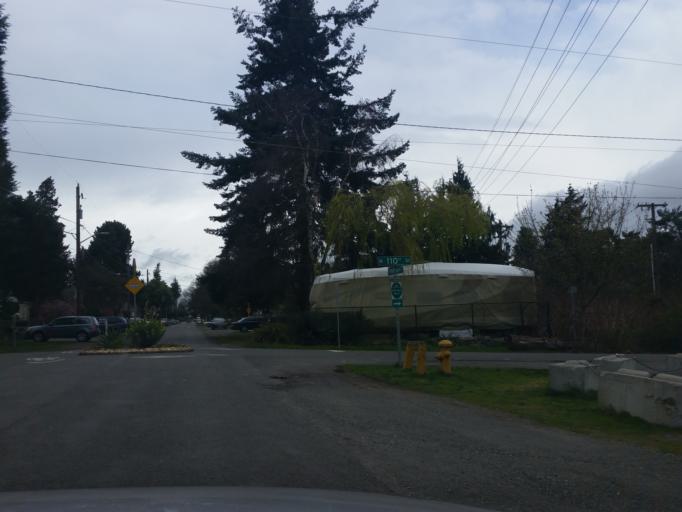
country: US
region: Washington
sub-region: King County
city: Shoreline
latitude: 47.7084
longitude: -122.3501
